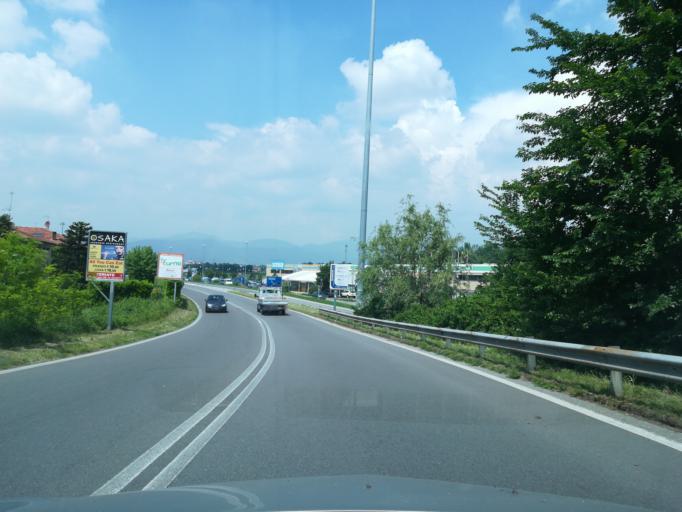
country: IT
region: Lombardy
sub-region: Provincia di Bergamo
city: Seriate
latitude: 45.6690
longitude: 9.7389
